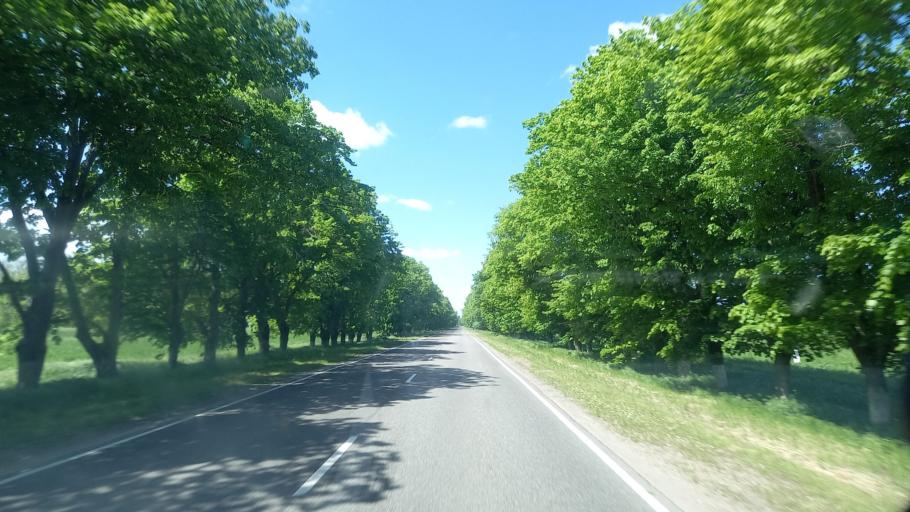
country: RU
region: Krasnodarskiy
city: Kazanskaya
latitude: 45.3706
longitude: 40.4403
